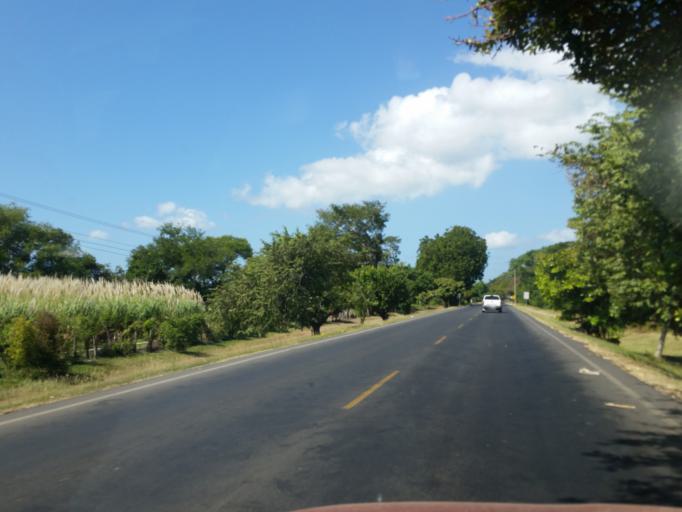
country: NI
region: Granada
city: Nandaime
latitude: 11.7531
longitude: -86.0404
